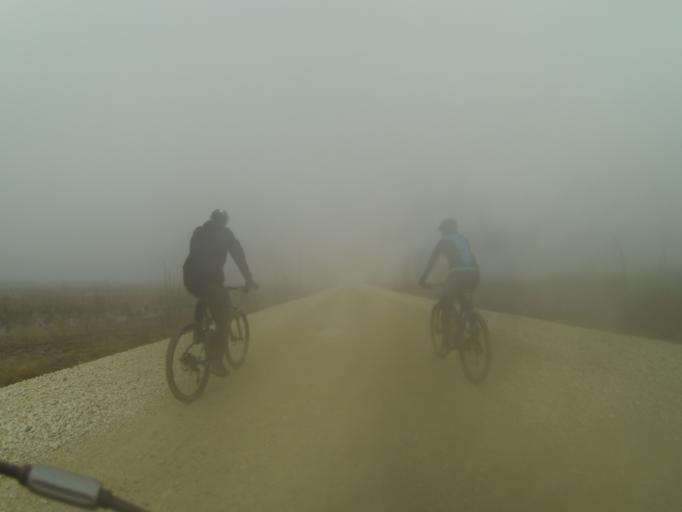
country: RO
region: Mehedinti
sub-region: Comuna Baclesu
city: Baclesu
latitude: 44.4618
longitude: 23.1147
